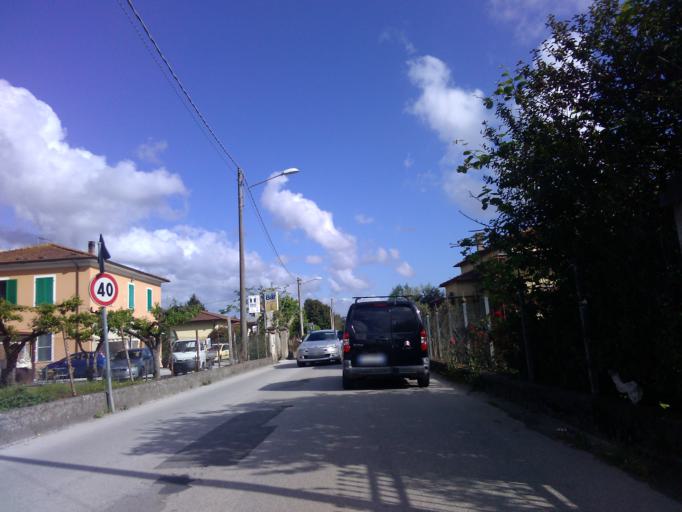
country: IT
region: Tuscany
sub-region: Provincia di Massa-Carrara
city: Capanne-Prato-Cinquale
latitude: 44.0101
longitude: 10.1442
